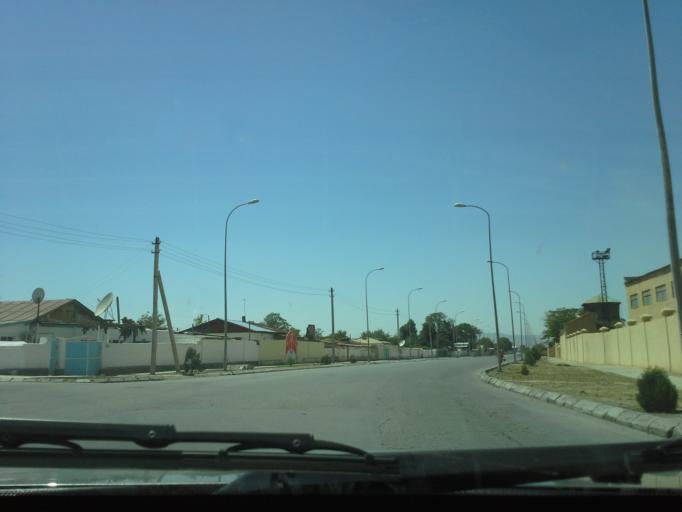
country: TM
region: Balkan
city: Serdar
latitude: 38.9772
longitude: 56.2740
